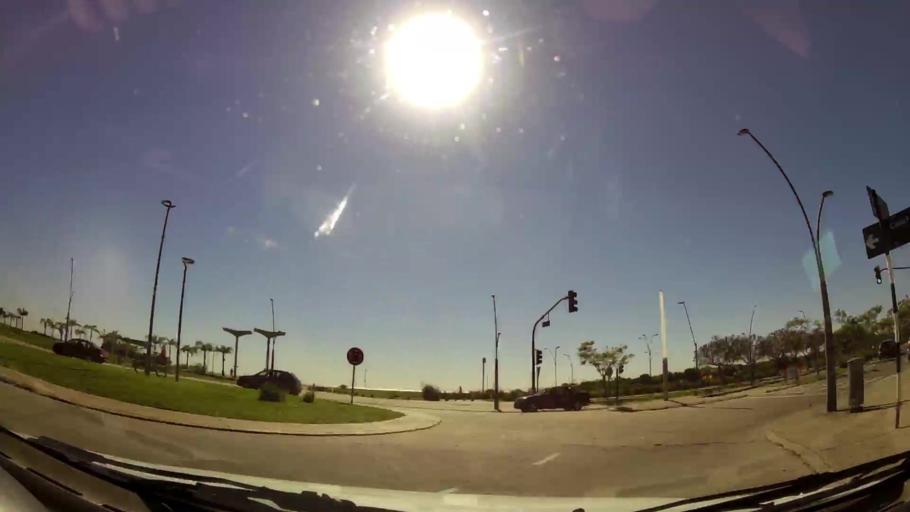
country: AR
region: Buenos Aires
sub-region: Partido de Vicente Lopez
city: Olivos
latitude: -34.5244
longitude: -58.4686
